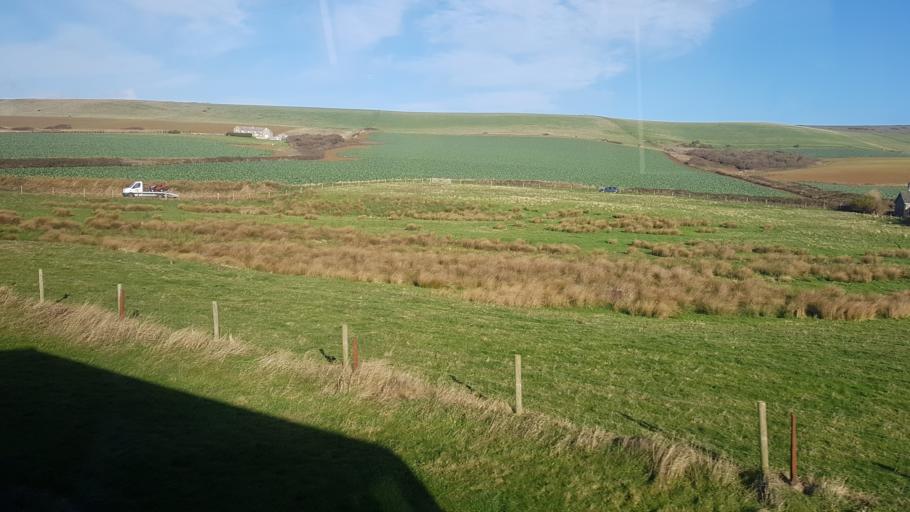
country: GB
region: England
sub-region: Isle of Wight
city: Freshwater
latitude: 50.6546
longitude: -1.4651
